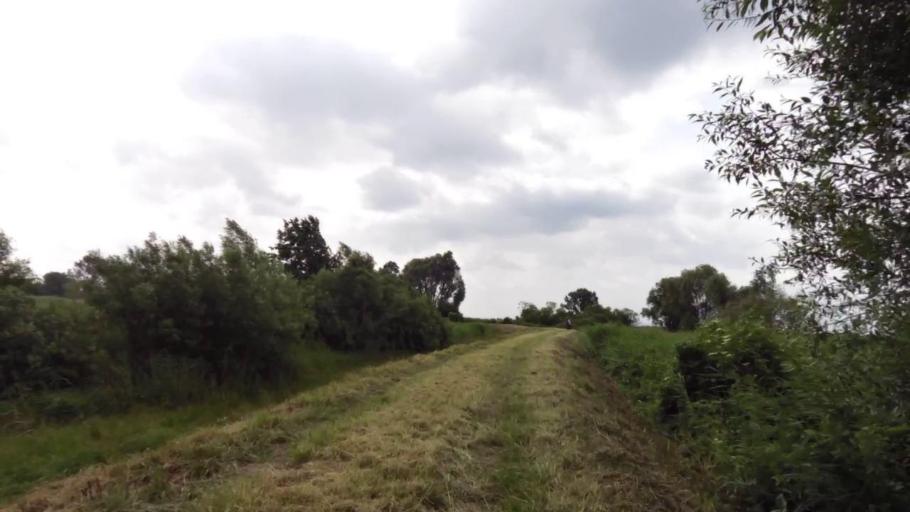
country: PL
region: West Pomeranian Voivodeship
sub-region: Powiat policki
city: Police
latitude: 53.5105
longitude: 14.6952
